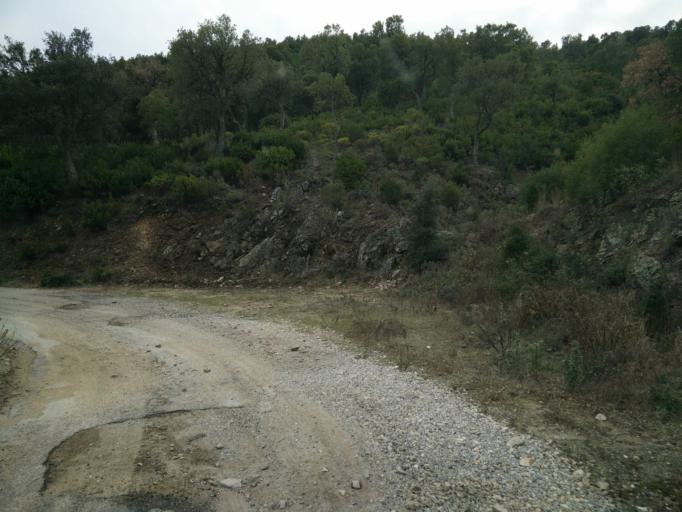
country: FR
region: Provence-Alpes-Cote d'Azur
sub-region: Departement du Var
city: Roquebrune-sur-Argens
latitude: 43.3936
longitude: 6.6086
